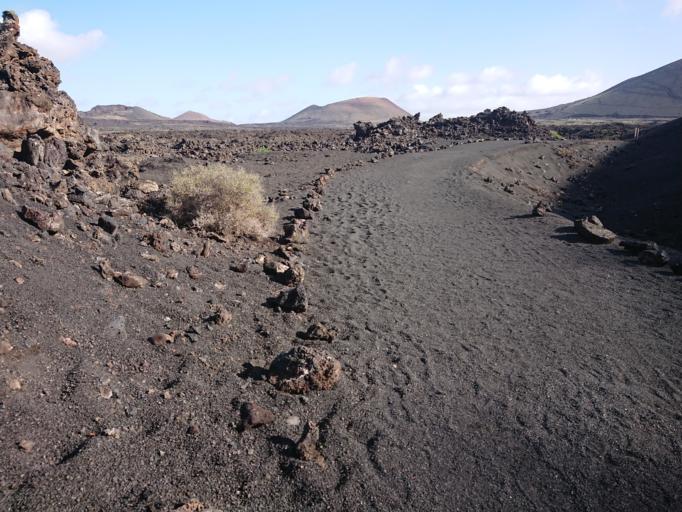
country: ES
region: Canary Islands
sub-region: Provincia de Las Palmas
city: Tias
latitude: 28.9929
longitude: -13.6943
